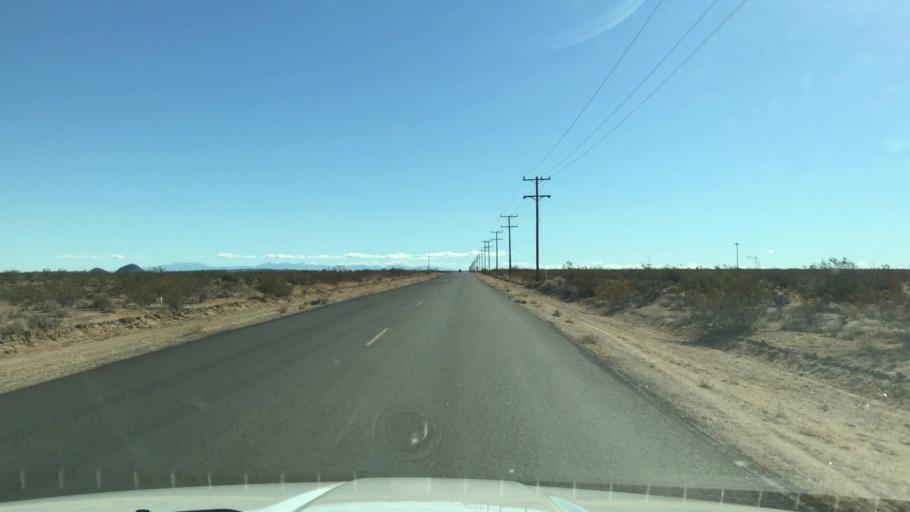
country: US
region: California
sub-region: Kern County
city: California City
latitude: 35.1873
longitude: -117.9858
